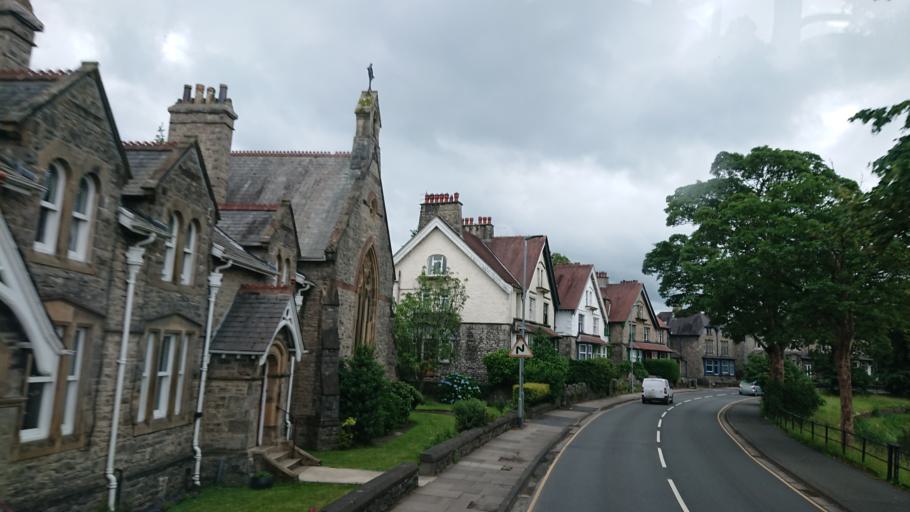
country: GB
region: England
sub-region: Cumbria
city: Kendal
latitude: 54.3234
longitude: -2.7423
